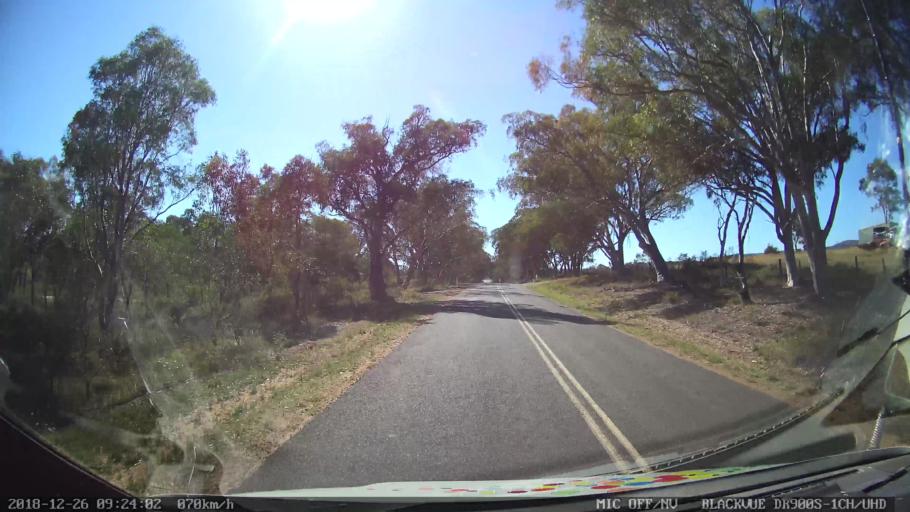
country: AU
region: New South Wales
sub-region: Mid-Western Regional
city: Kandos
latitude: -32.8089
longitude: 149.9939
